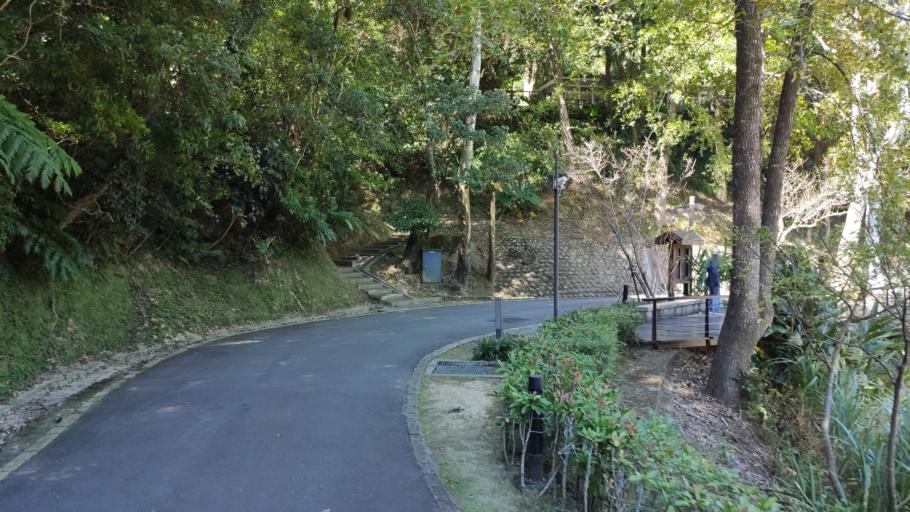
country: TW
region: Taiwan
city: Daxi
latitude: 24.8445
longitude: 121.3016
